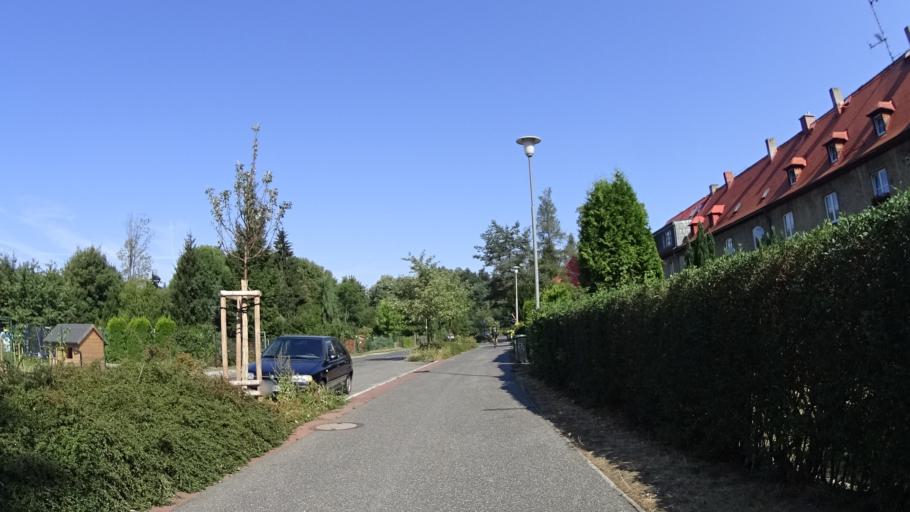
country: CZ
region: Liberecky
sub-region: Okres Liberec
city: Liberec
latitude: 50.7692
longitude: 15.0433
